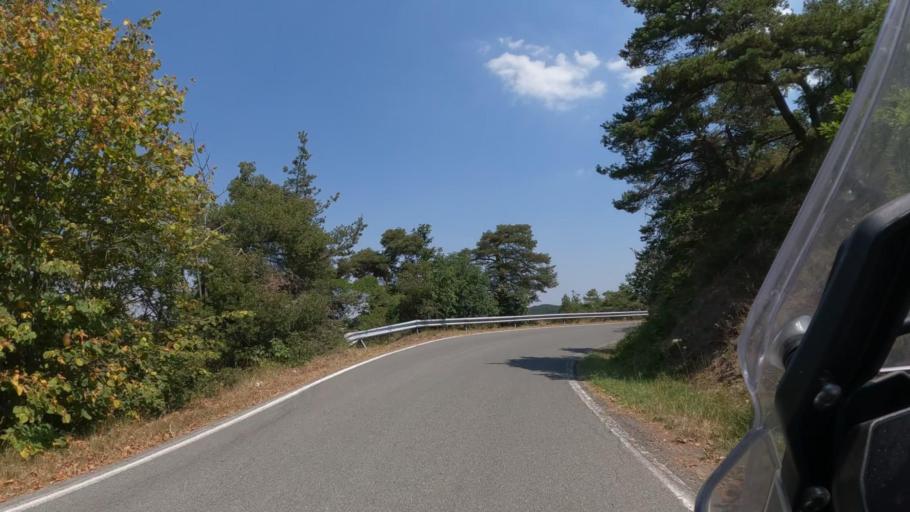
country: IT
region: Piedmont
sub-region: Provincia di Alessandria
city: Morbello
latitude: 44.5557
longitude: 8.5043
